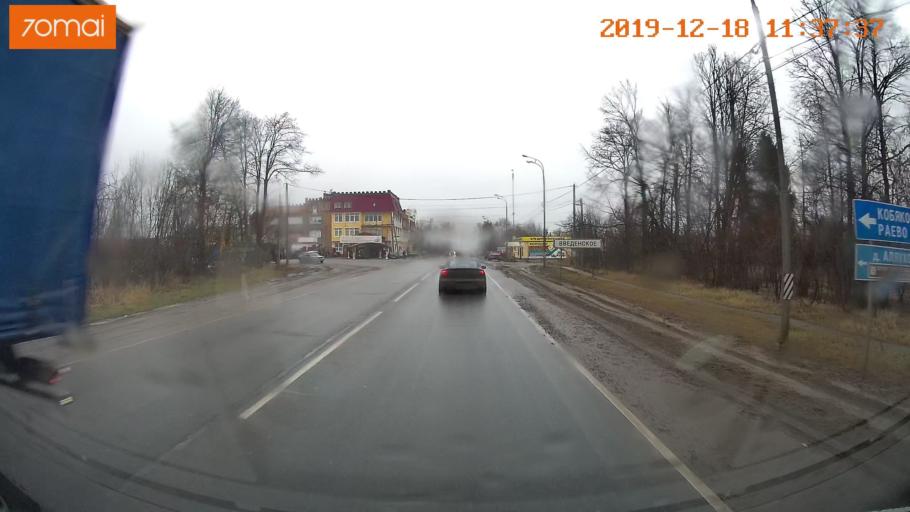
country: RU
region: Moskovskaya
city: Zvenigorod
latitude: 55.6913
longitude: 36.8942
